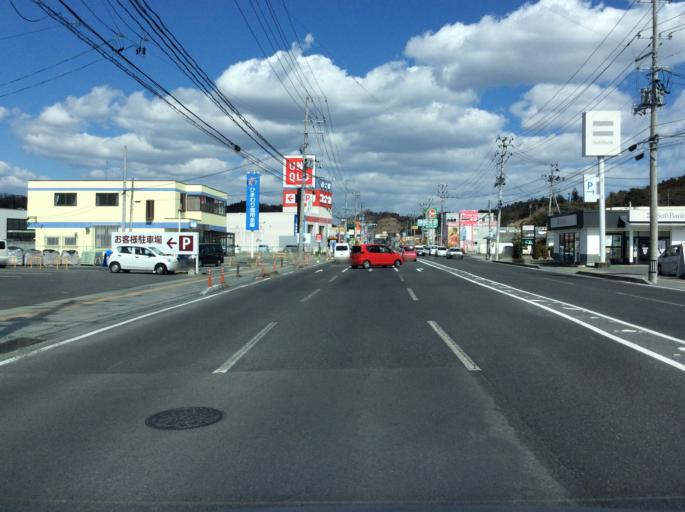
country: JP
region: Fukushima
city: Iwaki
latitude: 36.9611
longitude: 140.9041
